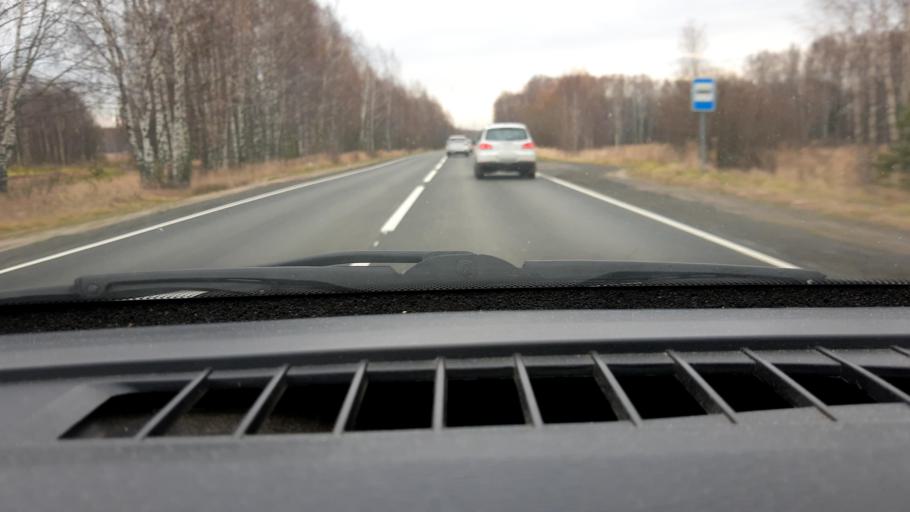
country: RU
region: Nizjnij Novgorod
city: Novaya Balakhna
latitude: 56.5911
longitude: 43.6603
